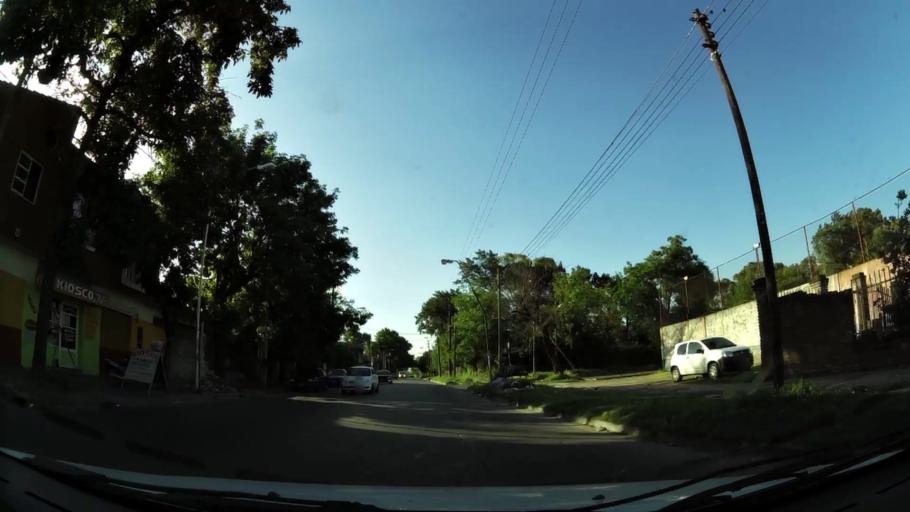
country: AR
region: Buenos Aires
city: Caseros
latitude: -34.5756
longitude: -58.5819
